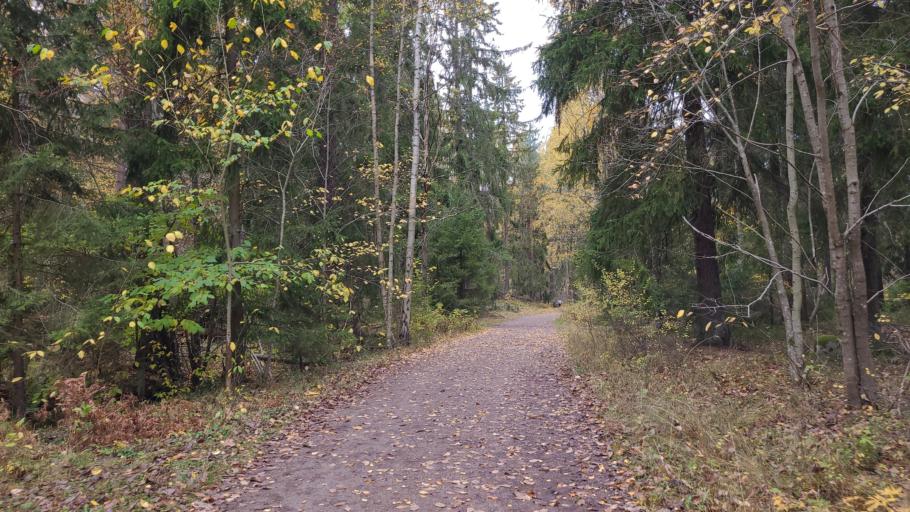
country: SE
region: Stockholm
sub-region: Solna Kommun
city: Rasunda
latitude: 59.3901
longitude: 17.9747
